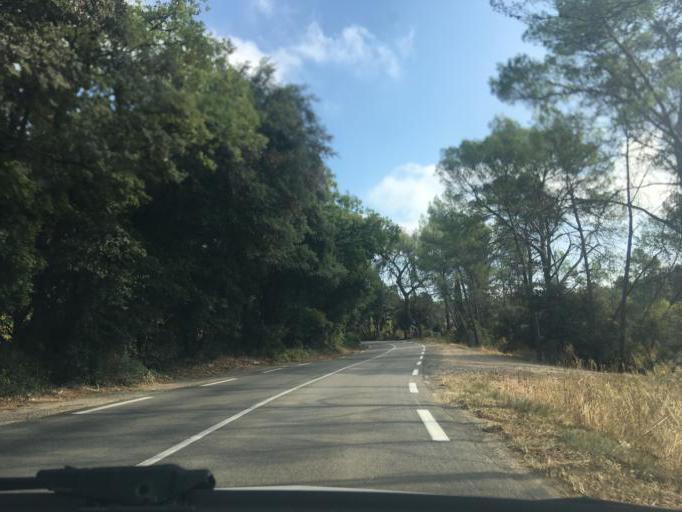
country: FR
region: Provence-Alpes-Cote d'Azur
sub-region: Departement du Var
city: Flayosc
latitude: 43.5072
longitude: 6.4221
